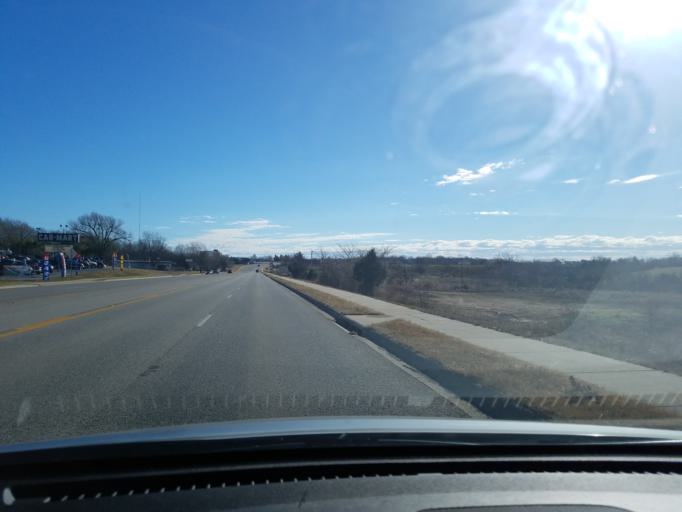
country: US
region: Arkansas
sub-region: Carroll County
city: Berryville
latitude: 36.3815
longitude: -93.5942
